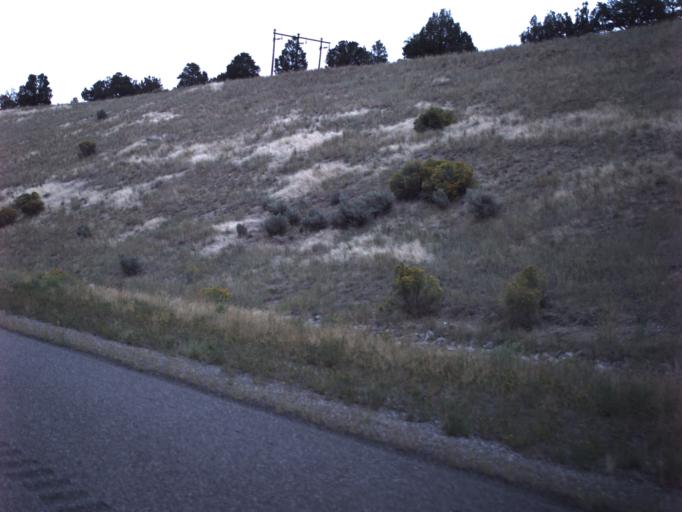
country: US
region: Utah
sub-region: Sevier County
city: Monroe
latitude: 38.5534
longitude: -112.3642
